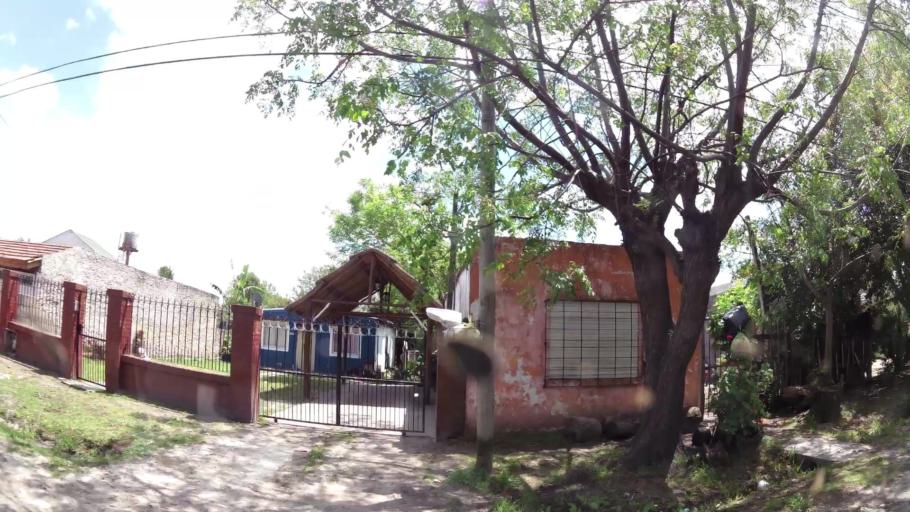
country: AR
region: Buenos Aires
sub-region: Partido de Quilmes
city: Quilmes
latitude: -34.8241
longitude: -58.2353
